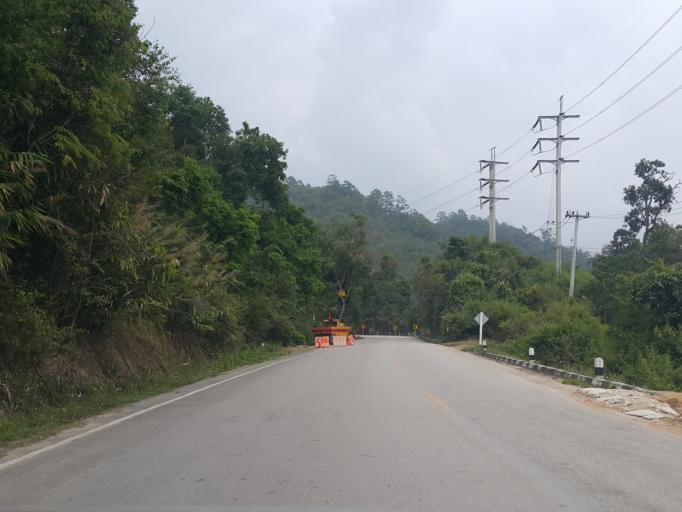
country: TH
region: Mae Hong Son
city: Mae Hi
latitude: 19.2699
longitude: 98.5376
